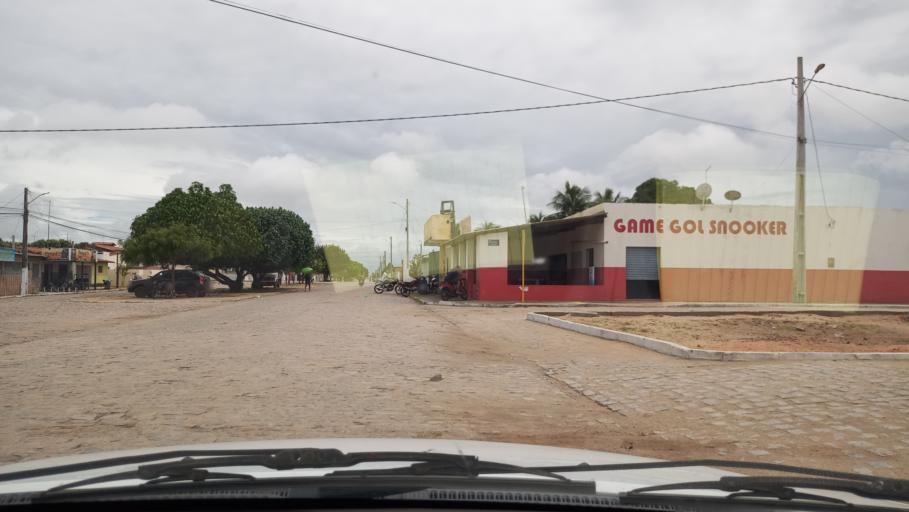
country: BR
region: Rio Grande do Norte
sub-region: Poco Branco
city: Poco Branco
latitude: -5.6198
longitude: -35.6587
